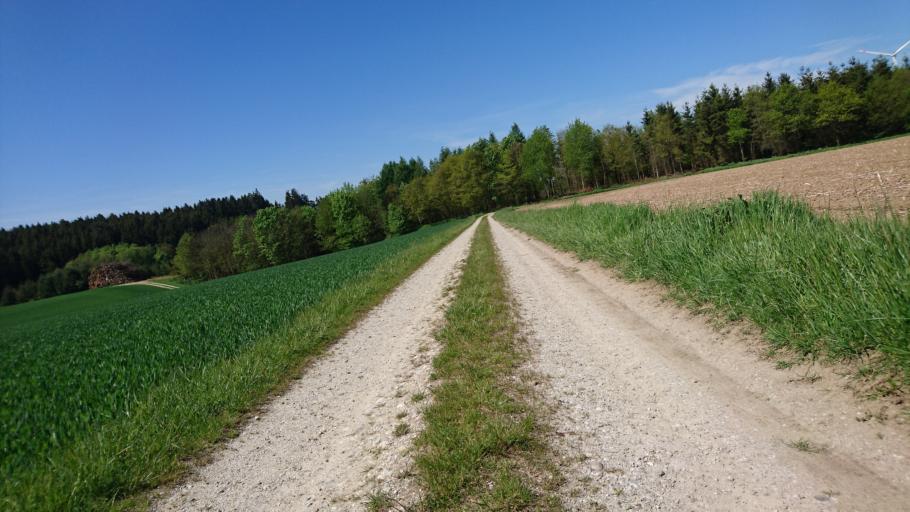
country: DE
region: Bavaria
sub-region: Lower Bavaria
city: Stallwang
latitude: 48.5310
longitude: 12.2282
